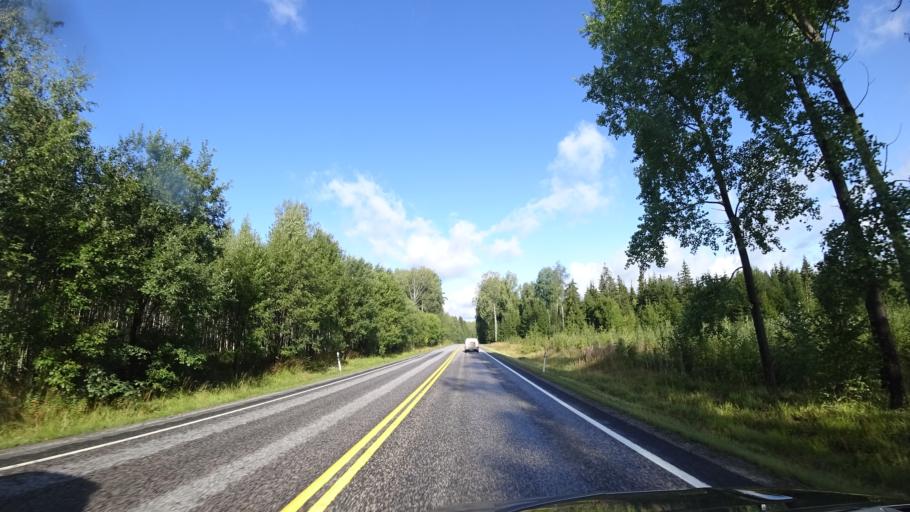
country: FI
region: Uusimaa
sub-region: Helsinki
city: Tuusula
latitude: 60.4479
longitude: 24.9637
